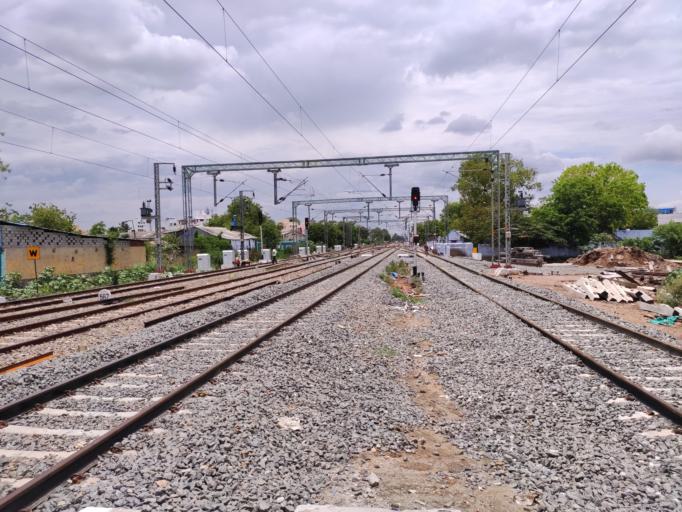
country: IN
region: Tamil Nadu
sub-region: Thoothukkudi
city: Kovilpatti
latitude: 9.1800
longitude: 77.8692
